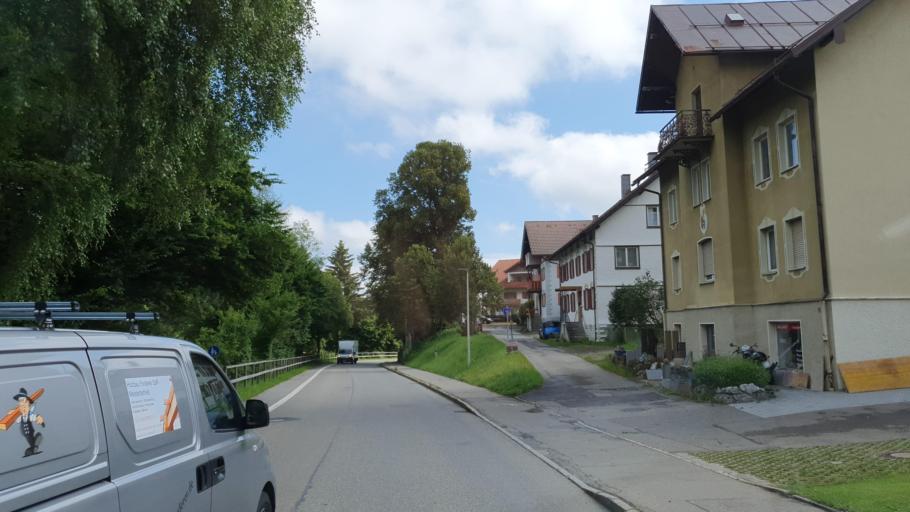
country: DE
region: Bavaria
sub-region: Swabia
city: Scheidegg
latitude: 47.5835
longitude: 9.8511
